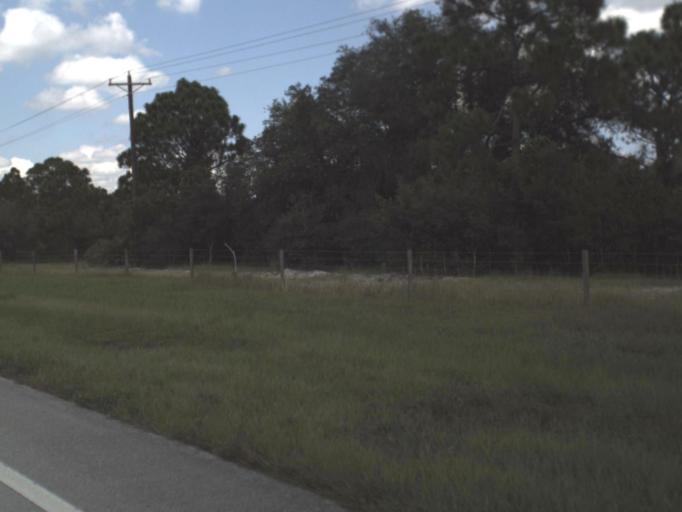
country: US
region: Florida
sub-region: Okeechobee County
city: Okeechobee
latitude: 27.3663
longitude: -81.0679
